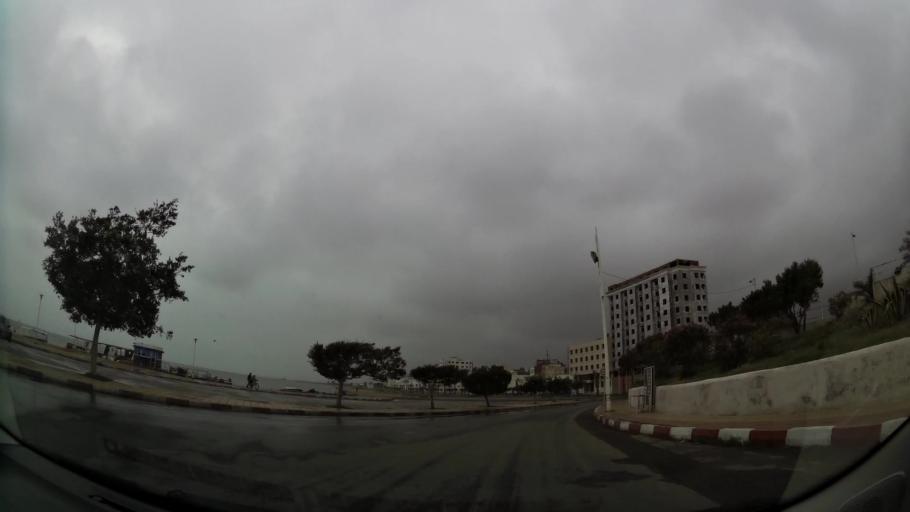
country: MA
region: Oriental
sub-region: Nador
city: Nador
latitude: 35.1855
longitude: -2.9250
